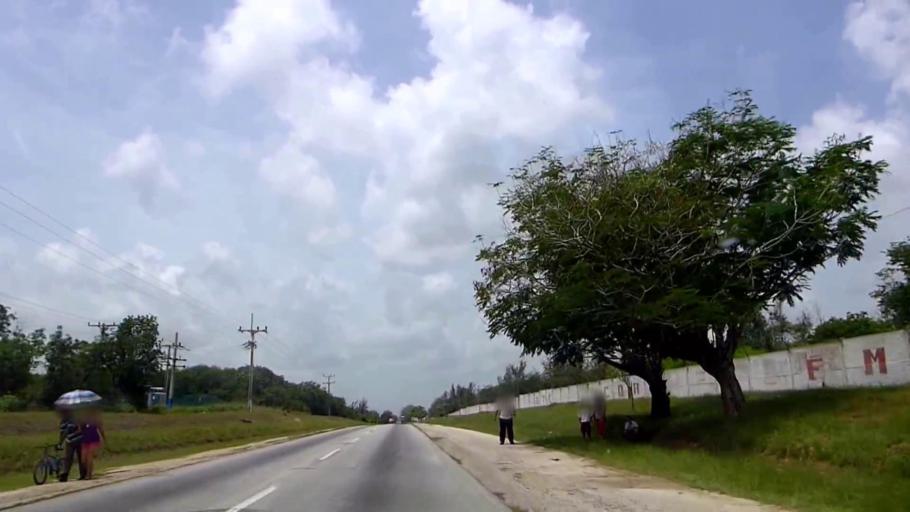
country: CU
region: Holguin
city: Cacocum
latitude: 20.7989
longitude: -76.2962
